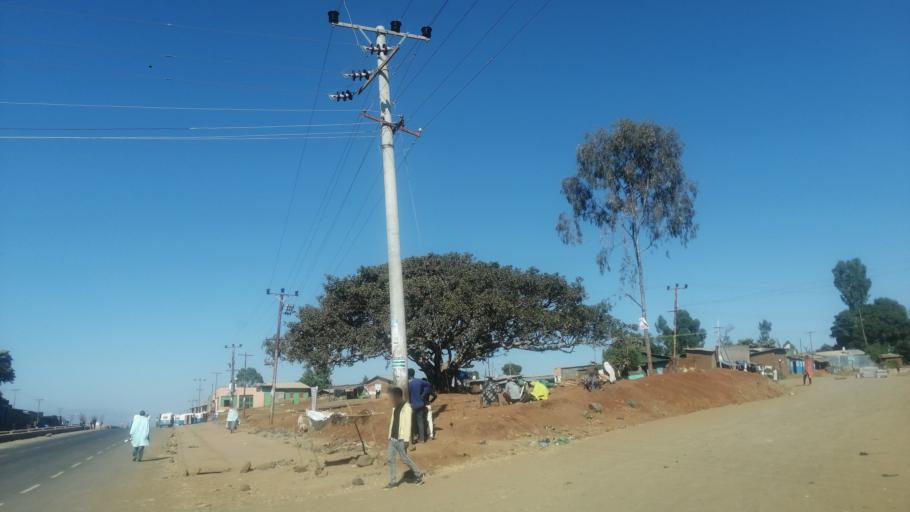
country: ET
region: Amhara
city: Addiet Canna
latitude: 11.0805
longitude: 37.8748
